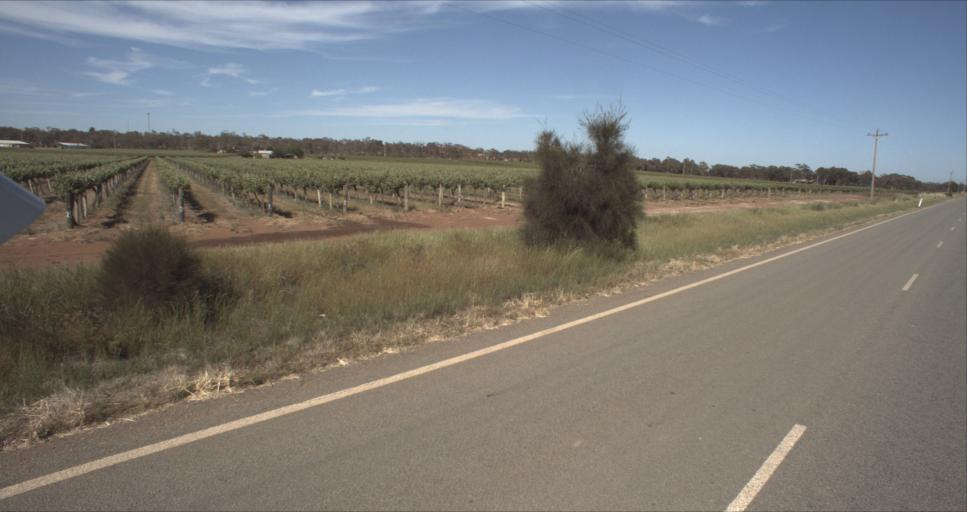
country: AU
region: New South Wales
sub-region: Leeton
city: Leeton
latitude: -34.5582
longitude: 146.4632
